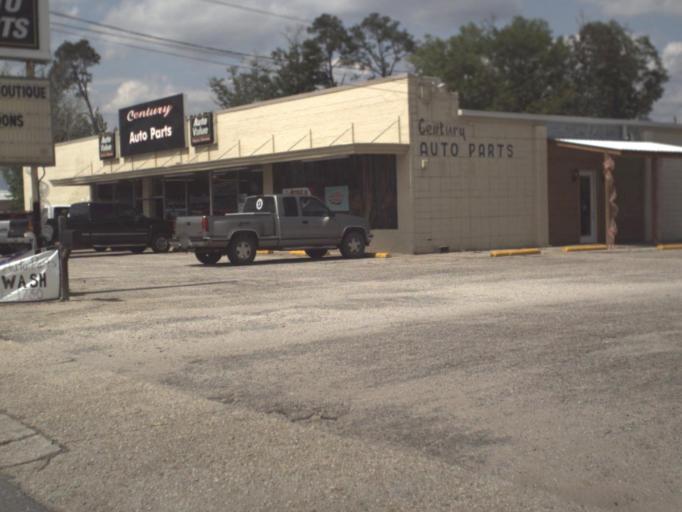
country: US
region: Alabama
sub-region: Escambia County
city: Flomaton
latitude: 30.9962
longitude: -87.2593
